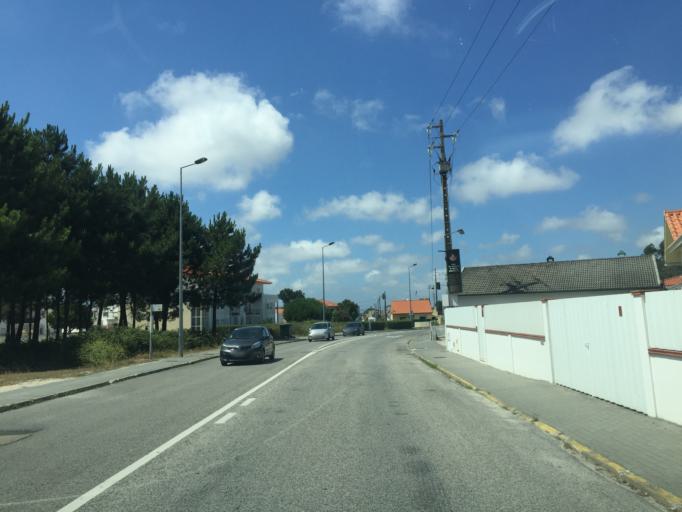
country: PT
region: Leiria
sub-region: Marinha Grande
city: Marinha Grande
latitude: 39.7297
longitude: -8.9301
